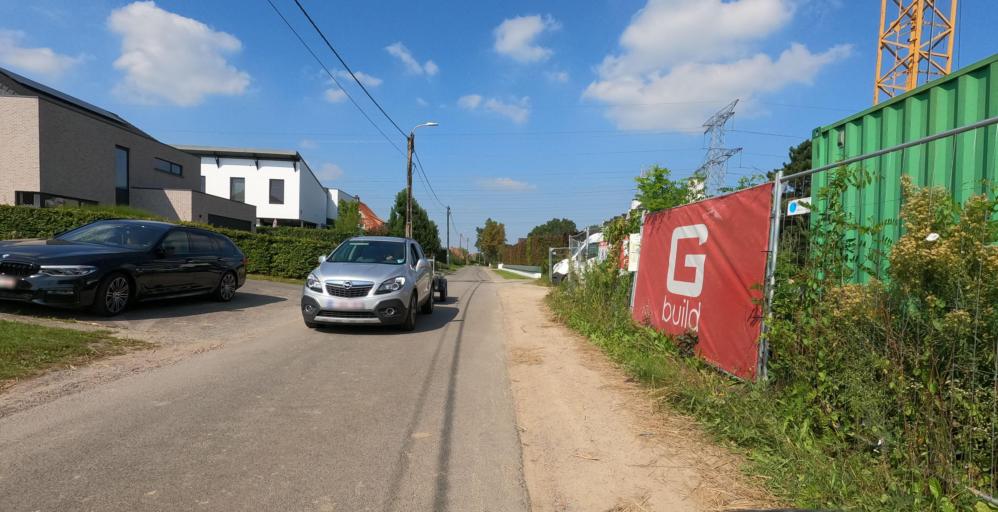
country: BE
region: Flanders
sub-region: Provincie Oost-Vlaanderen
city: Temse
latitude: 51.1383
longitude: 4.2257
